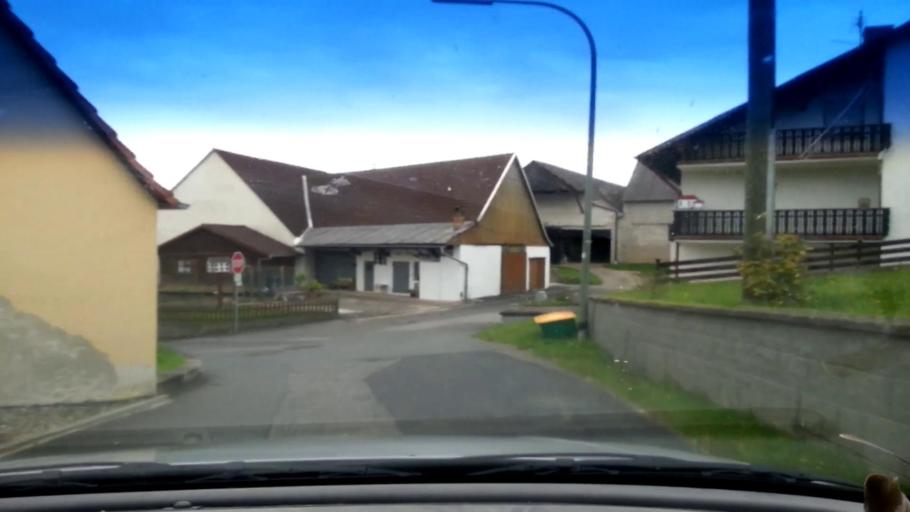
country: DE
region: Bavaria
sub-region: Upper Franconia
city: Priesendorf
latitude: 49.8668
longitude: 10.6547
